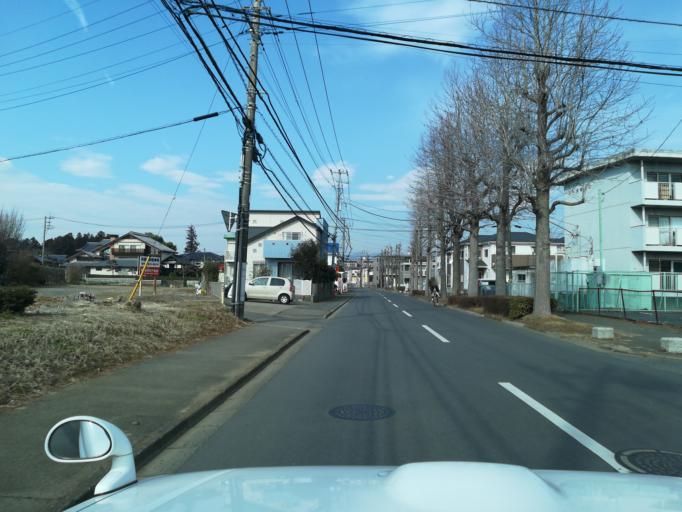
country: JP
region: Ibaraki
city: Naka
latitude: 36.0994
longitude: 140.0985
